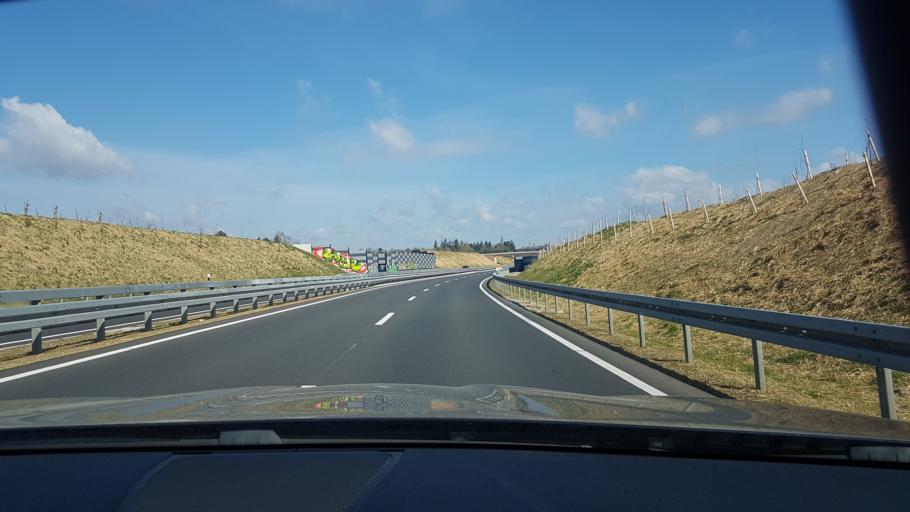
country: DE
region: Lower Saxony
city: Hemmingen
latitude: 52.3224
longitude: 9.7132
